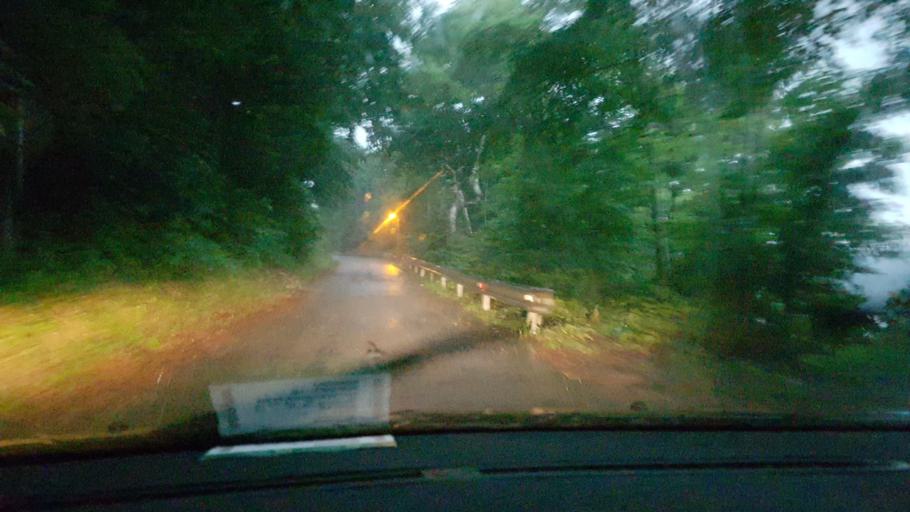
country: HR
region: Primorsko-Goranska
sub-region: Grad Delnice
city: Delnice
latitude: 45.3582
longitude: 14.7192
